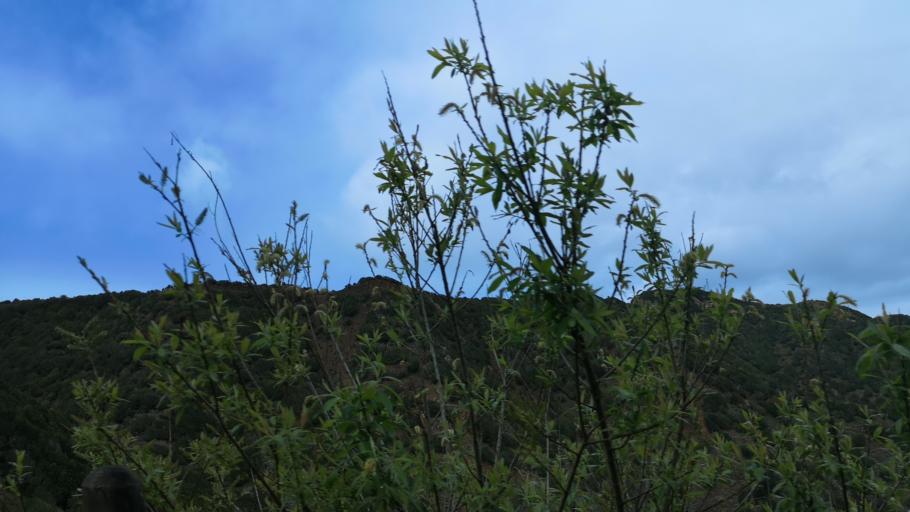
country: ES
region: Canary Islands
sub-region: Provincia de Santa Cruz de Tenerife
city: Vallehermosa
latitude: 28.1628
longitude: -17.2913
